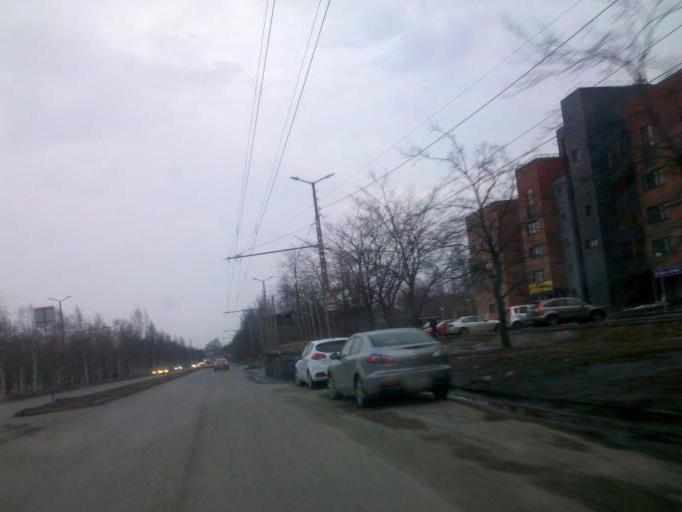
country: RU
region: Republic of Karelia
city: Petrozavodsk
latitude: 61.8061
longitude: 34.3419
